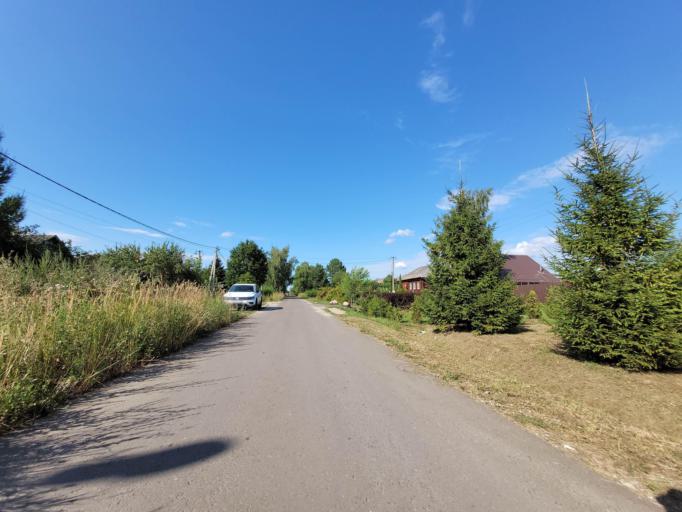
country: RU
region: Moskovskaya
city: Lopatinskiy
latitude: 55.3885
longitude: 38.7132
